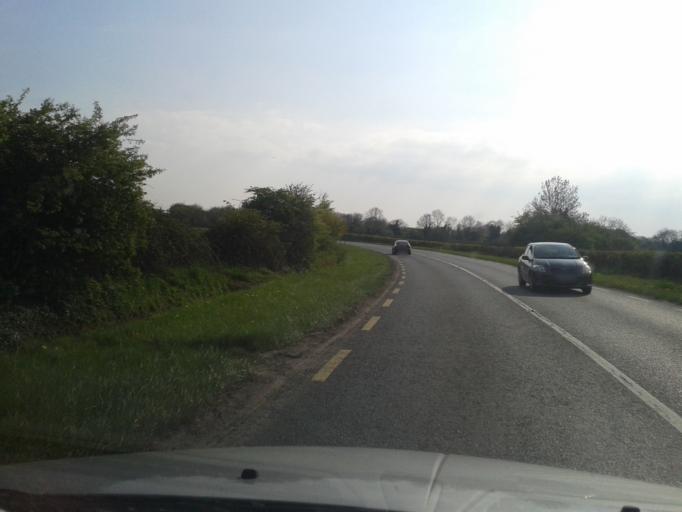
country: IE
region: Leinster
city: Ballymun
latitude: 53.4389
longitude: -6.2896
